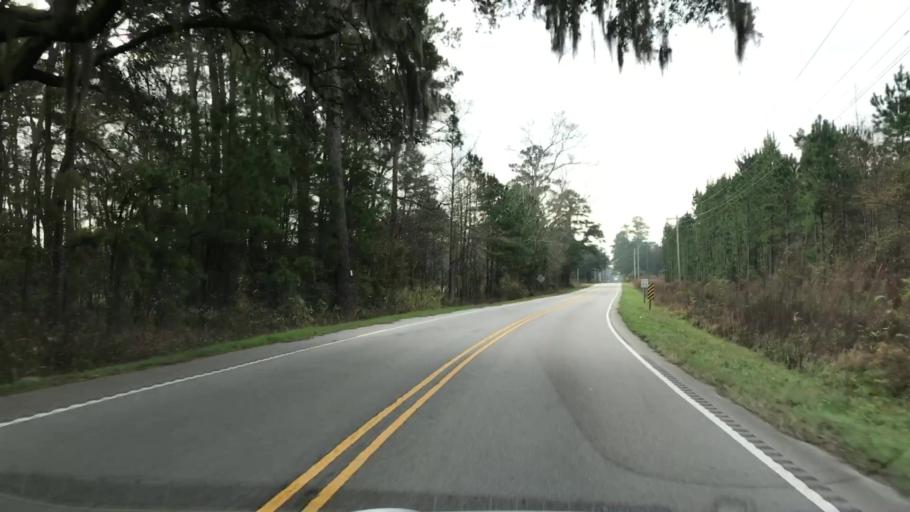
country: US
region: South Carolina
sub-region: Jasper County
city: Ridgeland
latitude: 32.5206
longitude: -80.8908
